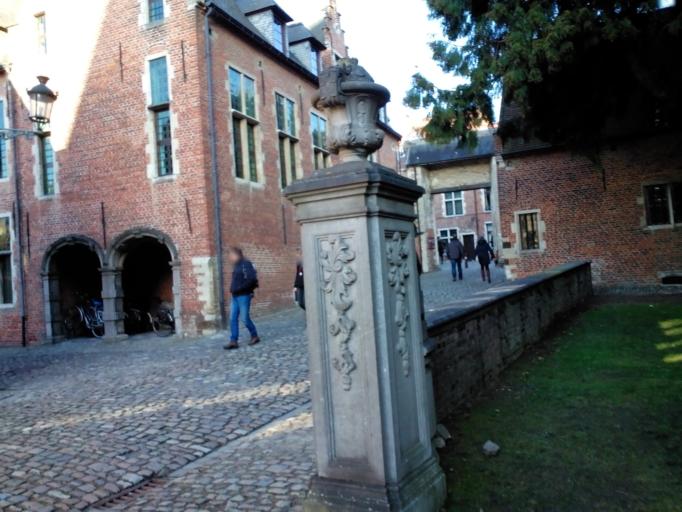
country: BE
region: Flanders
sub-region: Provincie Vlaams-Brabant
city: Leuven
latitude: 50.8716
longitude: 4.6975
